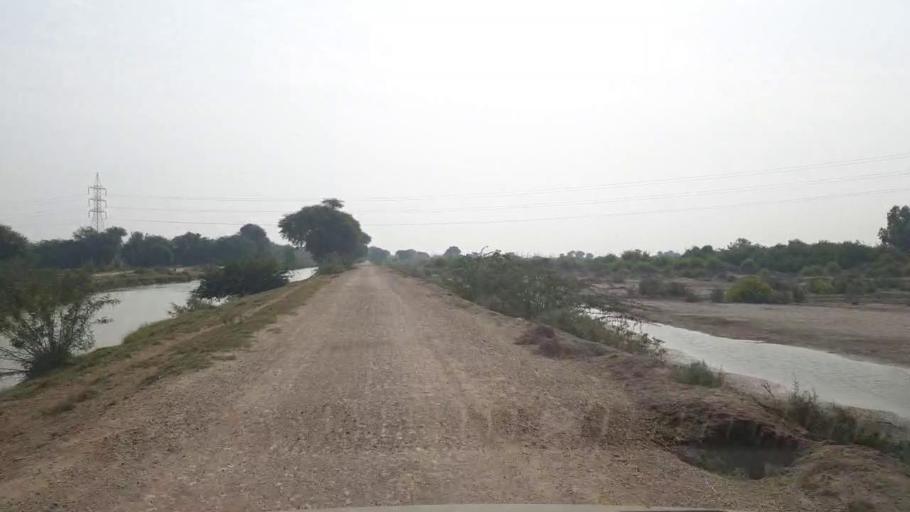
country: PK
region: Sindh
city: Tando Muhammad Khan
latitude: 25.1270
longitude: 68.4357
